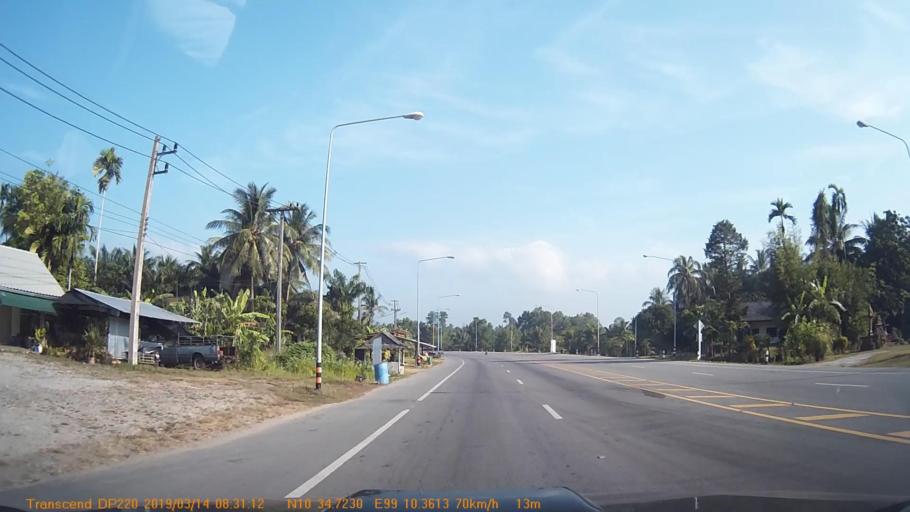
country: TH
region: Chumphon
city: Chumphon
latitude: 10.5785
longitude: 99.1727
